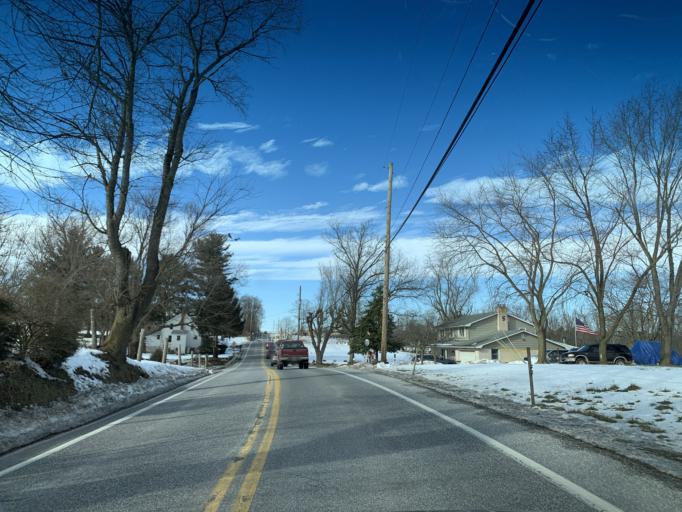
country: US
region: Pennsylvania
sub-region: York County
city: Weigelstown
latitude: 39.9473
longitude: -76.8297
